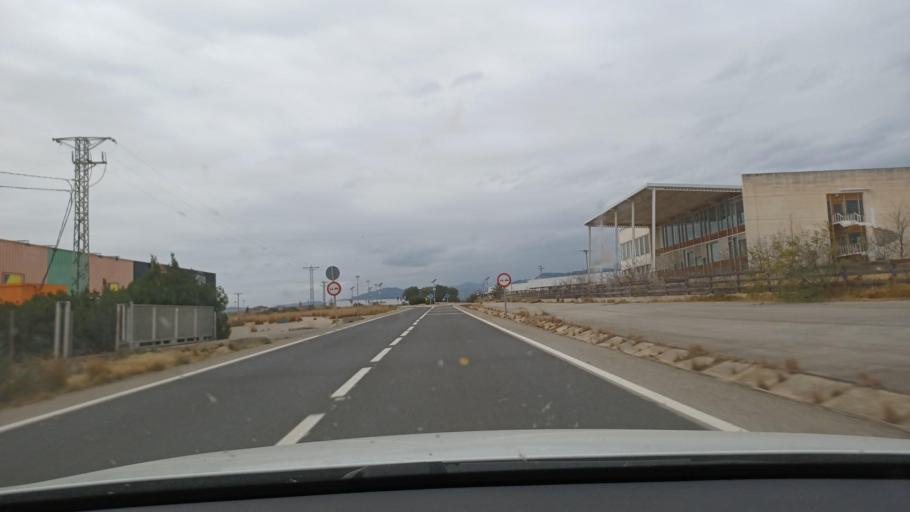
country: ES
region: Valencia
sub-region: Provincia de Castello
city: Rosell
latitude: 40.6348
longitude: 0.3155
